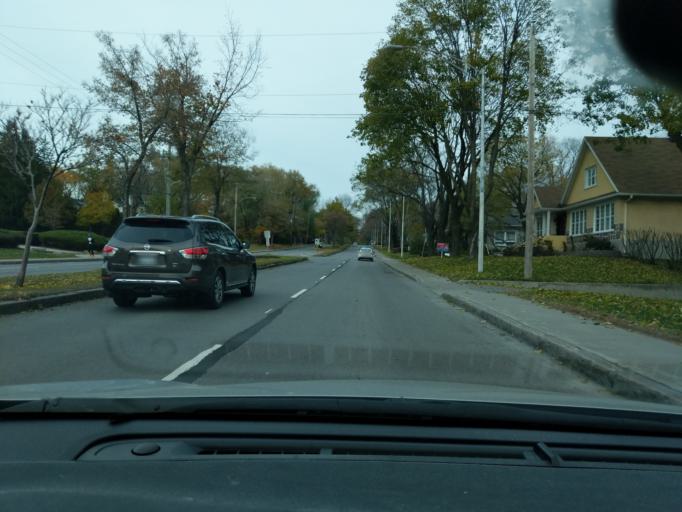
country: CA
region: Quebec
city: Quebec
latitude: 46.7913
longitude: -71.2427
